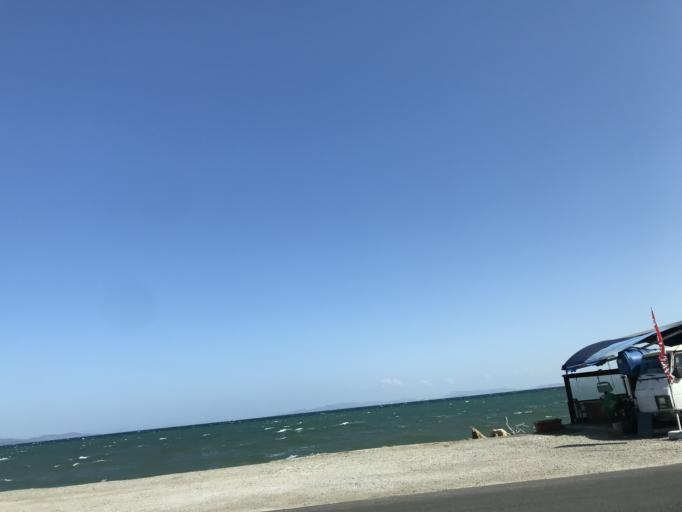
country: TR
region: Izmir
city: Urla
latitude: 38.3742
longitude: 26.8678
